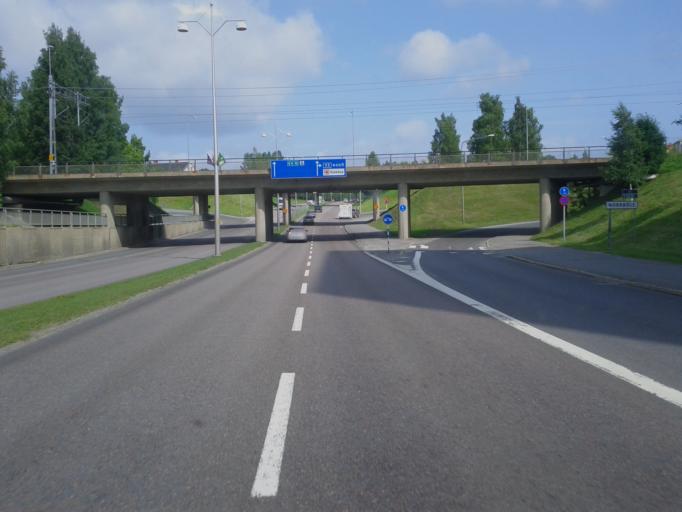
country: SE
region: Vaesterbotten
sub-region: Skelleftea Kommun
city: Skelleftea
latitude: 64.7522
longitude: 20.9616
